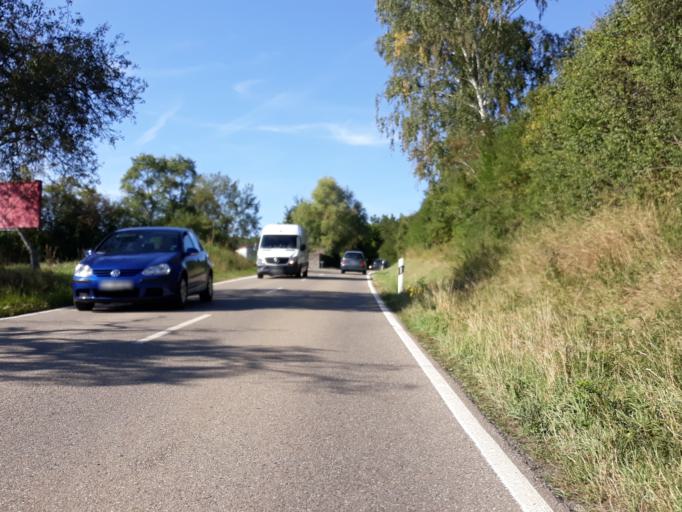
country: DE
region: Baden-Wuerttemberg
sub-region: Regierungsbezirk Stuttgart
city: Weil der Stadt
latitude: 48.7223
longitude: 8.8776
